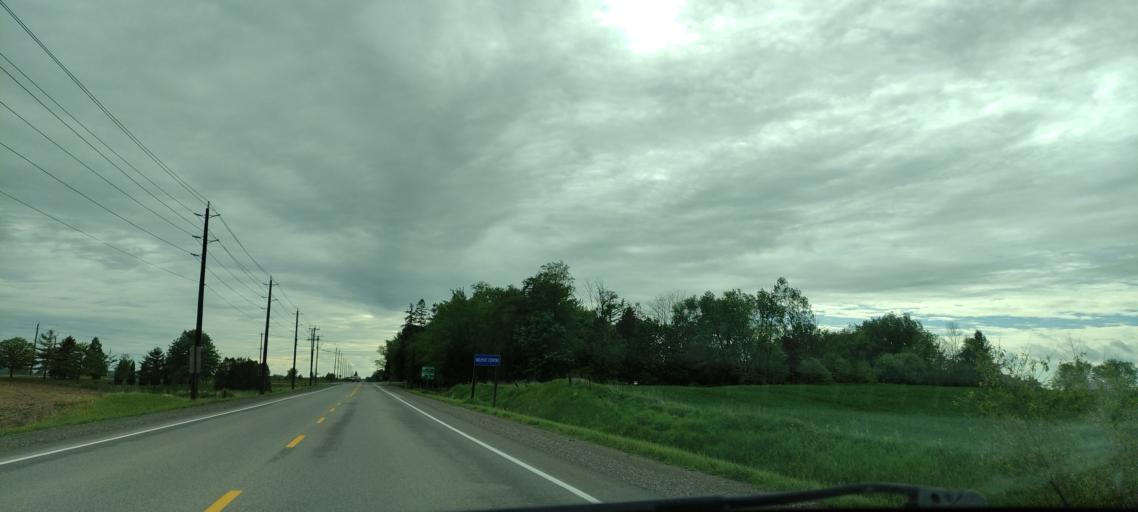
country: CA
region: Ontario
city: Kitchener
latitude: 43.3839
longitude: -80.6397
